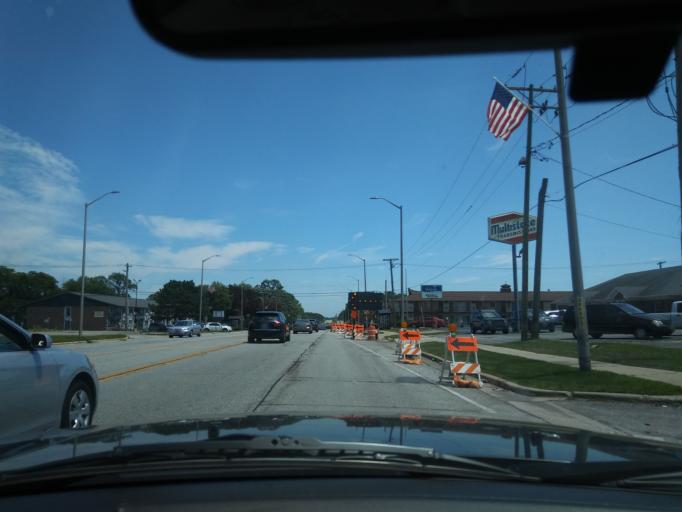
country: US
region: Illinois
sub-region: Cook County
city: Oak Forest
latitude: 41.6030
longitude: -87.7449
